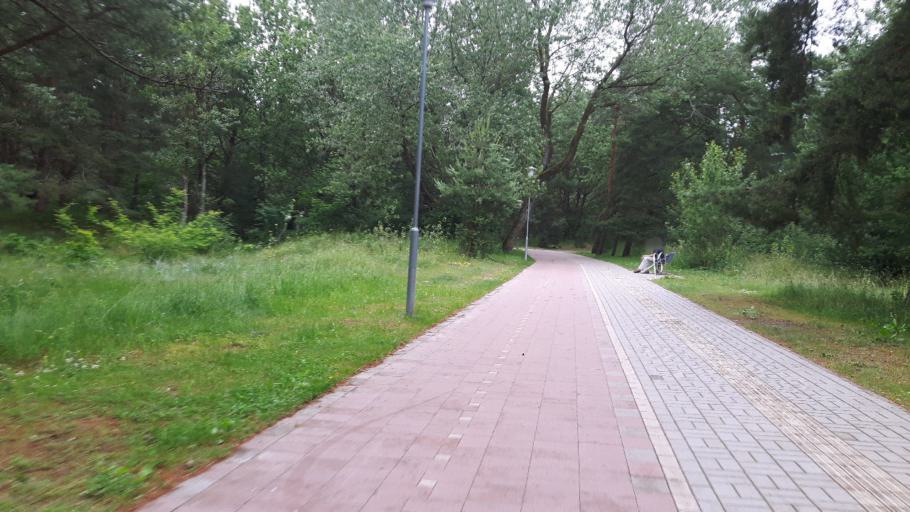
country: LV
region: Liepaja
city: Liepaja
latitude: 56.4850
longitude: 21.0017
